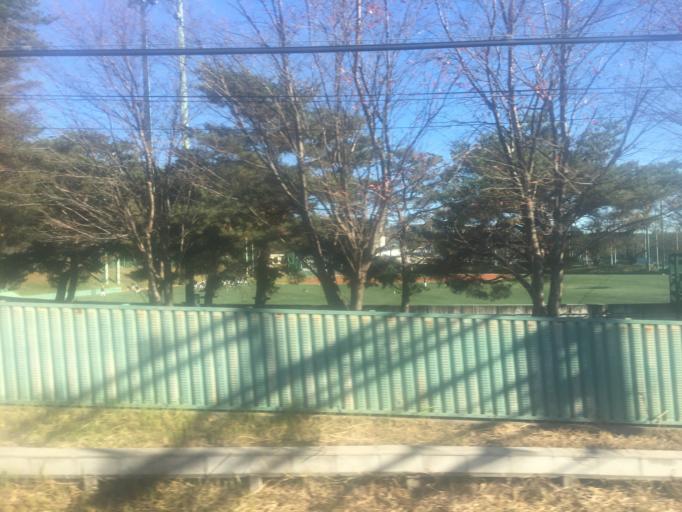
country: JP
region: Saitama
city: Sakado
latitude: 35.9332
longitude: 139.4297
